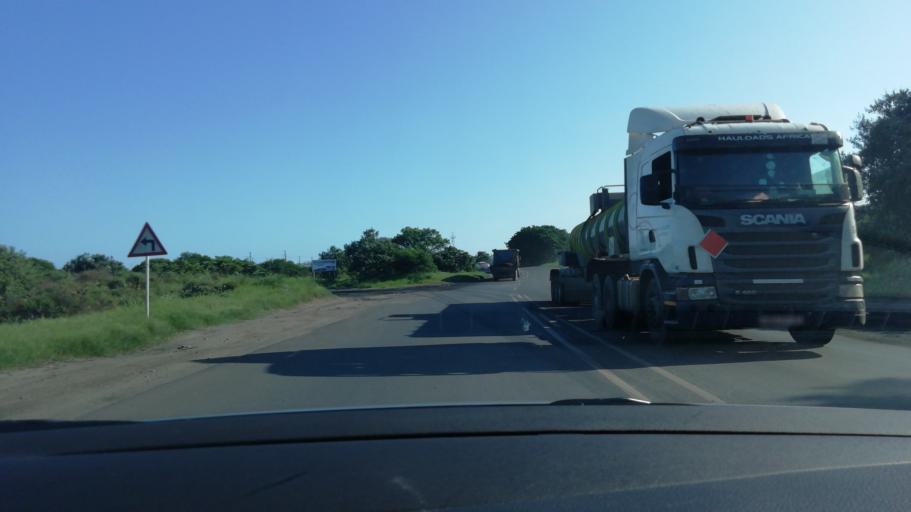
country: ZA
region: KwaZulu-Natal
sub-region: uThungulu District Municipality
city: Richards Bay
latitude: -28.7755
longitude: 32.0156
